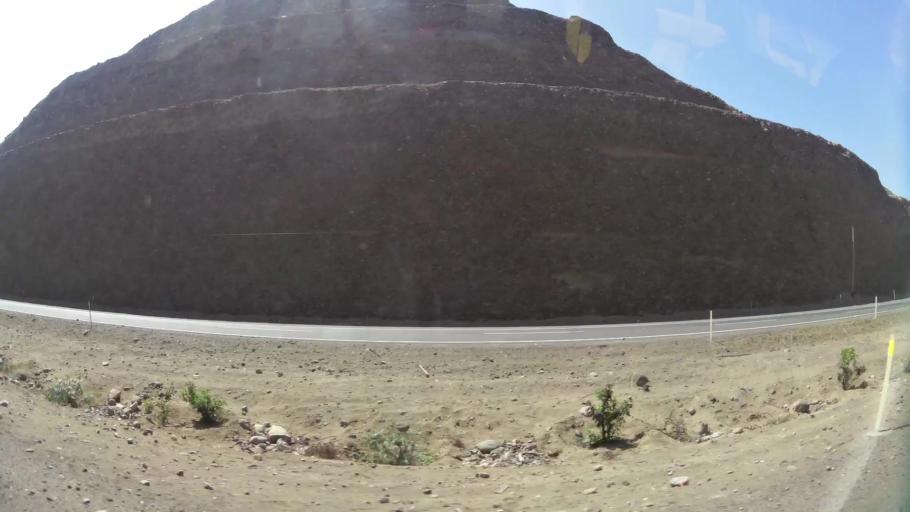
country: PE
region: Lima
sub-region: Provincia de Canete
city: Asia
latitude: -12.8072
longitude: -76.5434
